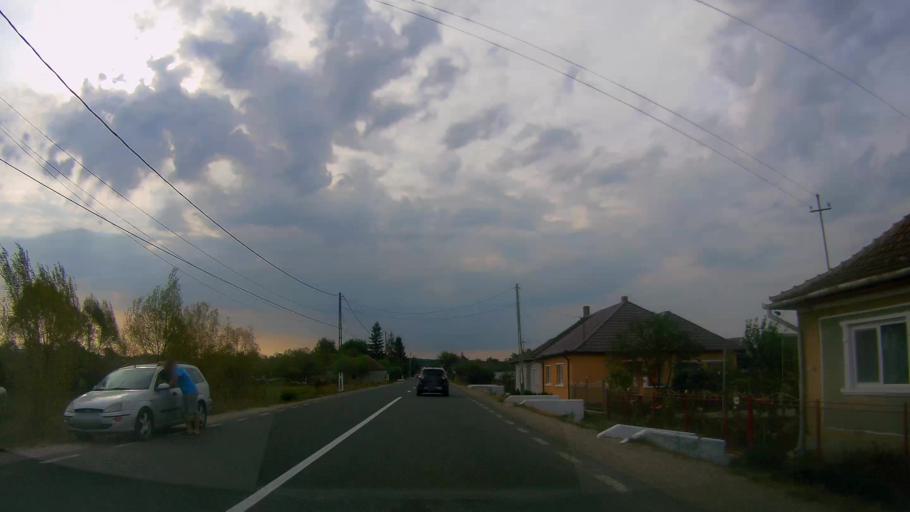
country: RO
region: Satu Mare
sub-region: Oras Ardud
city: Ardud
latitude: 47.5882
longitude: 22.8836
